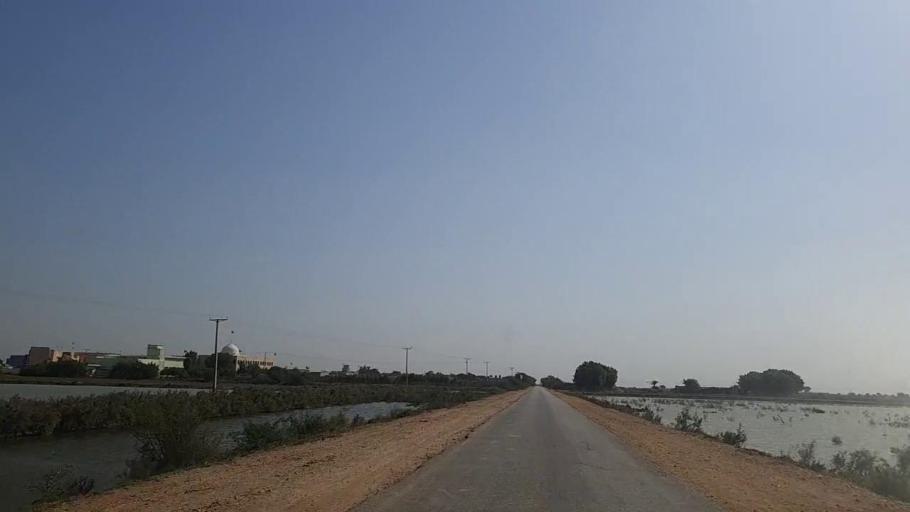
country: PK
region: Sindh
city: Mirpur Batoro
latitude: 24.6430
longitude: 68.2903
